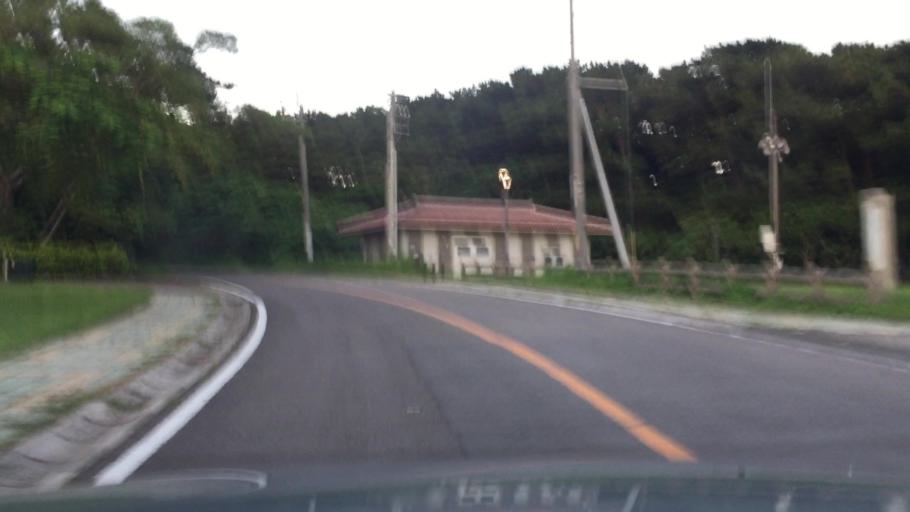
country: JP
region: Okinawa
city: Ishigaki
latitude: 24.3685
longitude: 124.1585
